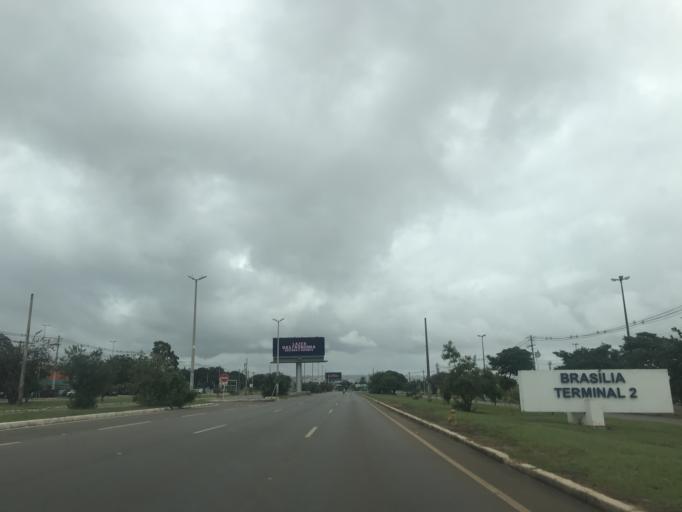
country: BR
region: Federal District
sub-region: Brasilia
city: Brasilia
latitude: -15.8706
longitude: -47.9298
